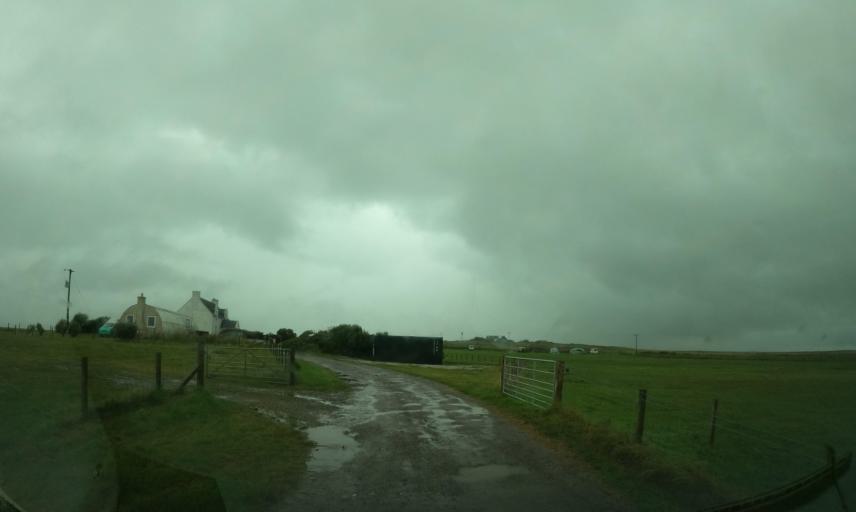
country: GB
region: Scotland
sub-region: Eilean Siar
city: Barra
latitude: 56.4771
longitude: -6.9211
